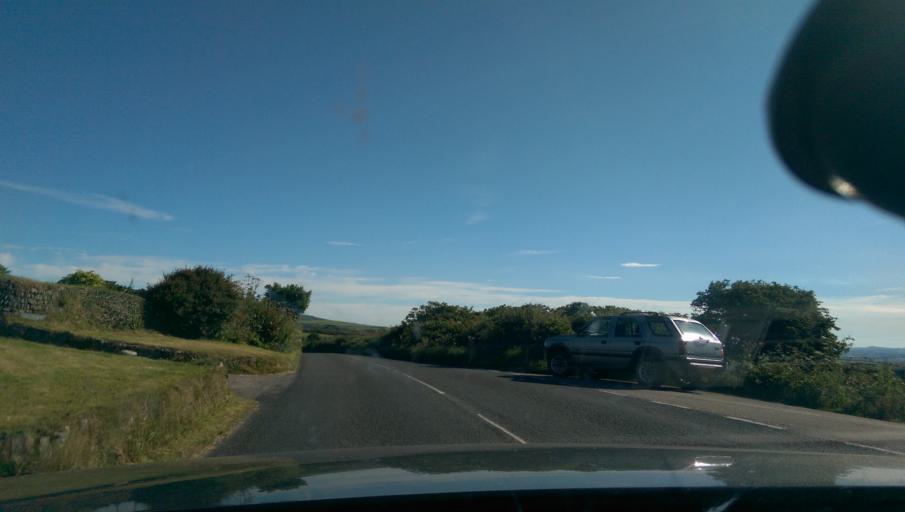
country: GB
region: England
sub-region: Cornwall
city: Penzance
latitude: 50.1548
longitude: -5.5139
